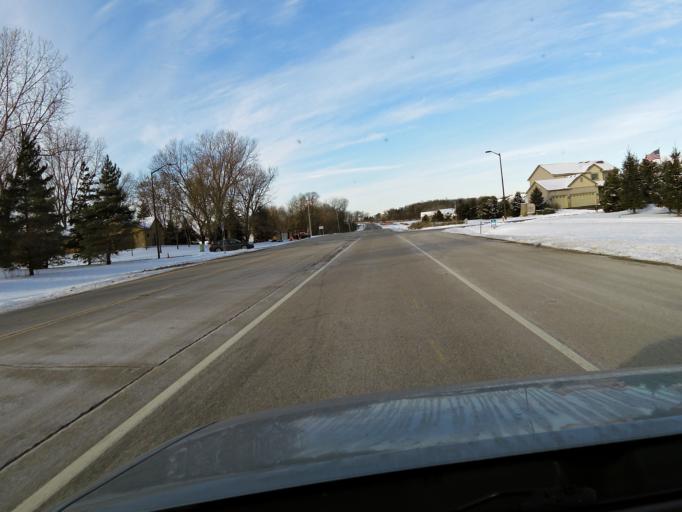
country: US
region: Minnesota
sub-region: Scott County
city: Prior Lake
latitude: 44.7652
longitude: -93.4192
